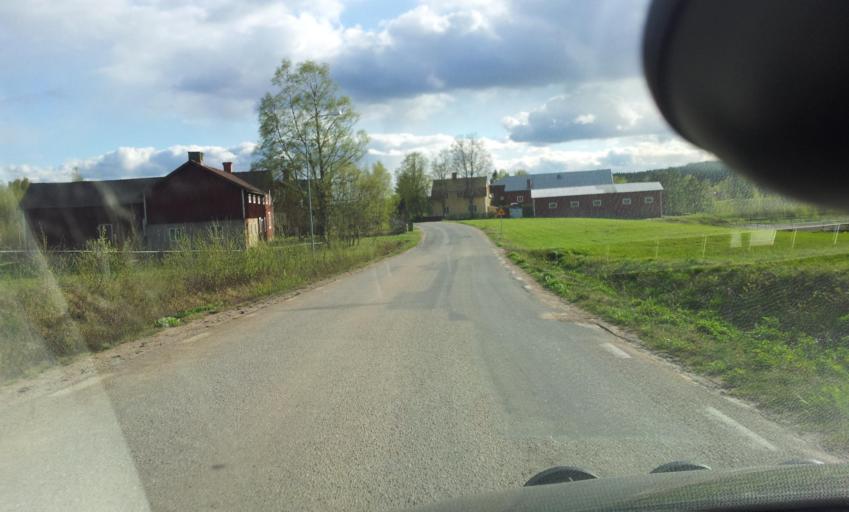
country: SE
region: Gaevleborg
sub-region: Bollnas Kommun
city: Kilafors
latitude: 61.3741
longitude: 16.6195
